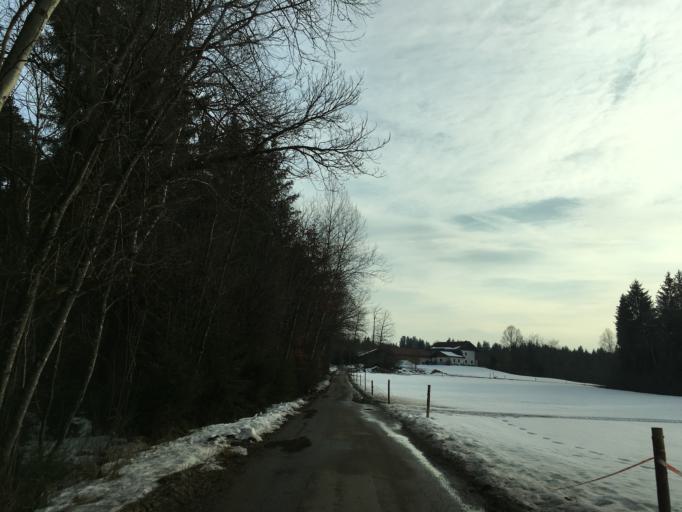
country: DE
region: Bavaria
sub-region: Upper Bavaria
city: Halfing
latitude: 47.9294
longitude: 12.2590
